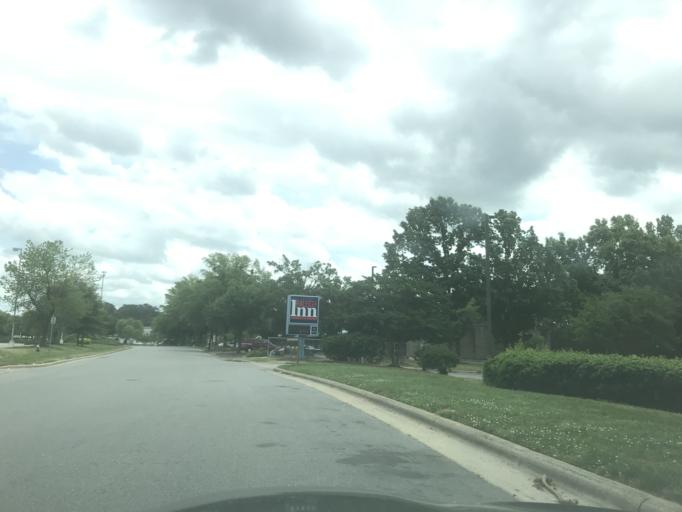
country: US
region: North Carolina
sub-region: Wake County
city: Raleigh
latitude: 35.7968
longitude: -78.5833
